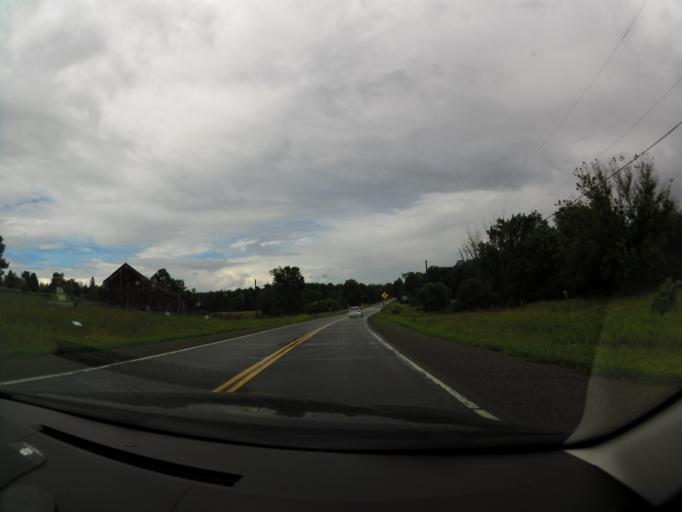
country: CA
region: Ontario
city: Perth
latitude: 45.0872
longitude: -76.4287
